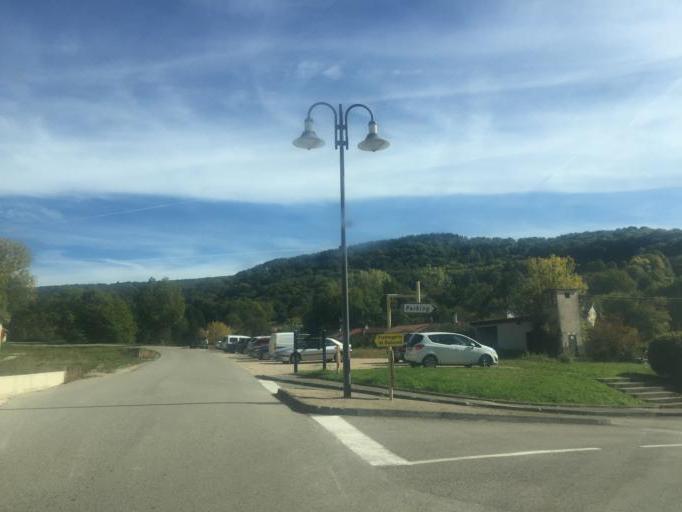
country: FR
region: Franche-Comte
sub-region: Departement du Jura
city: Saint-Amour
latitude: 46.4559
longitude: 5.3565
